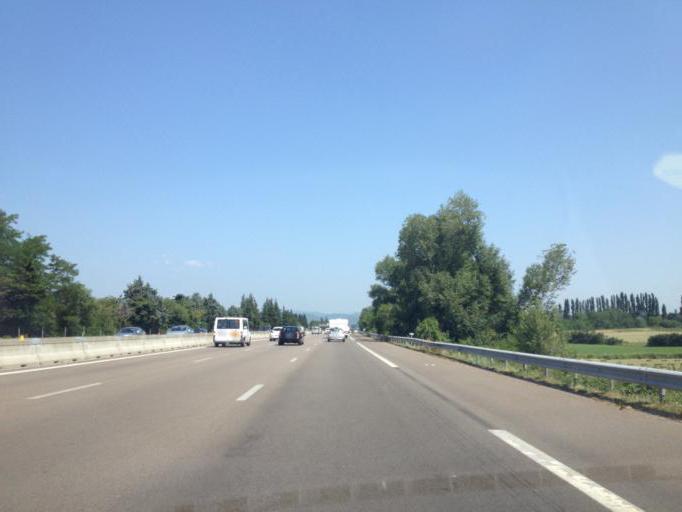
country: FR
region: Rhone-Alpes
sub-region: Departement de la Drome
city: Saulce-sur-Rhone
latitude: 44.6969
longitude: 4.7885
